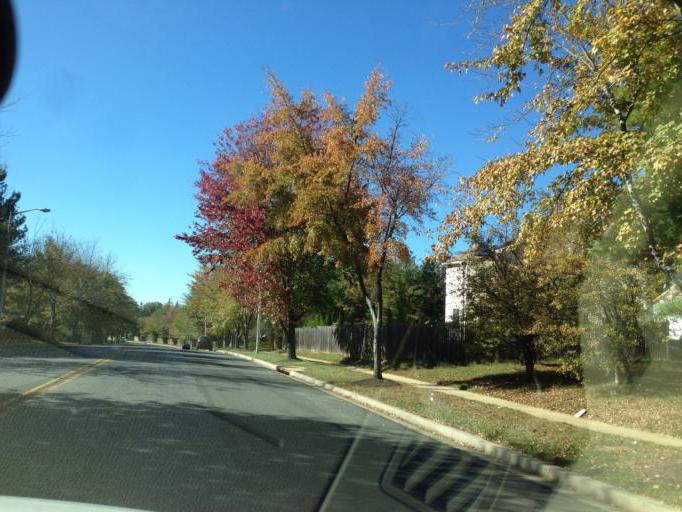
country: US
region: Maryland
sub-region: Montgomery County
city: Germantown
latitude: 39.1980
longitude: -77.2409
